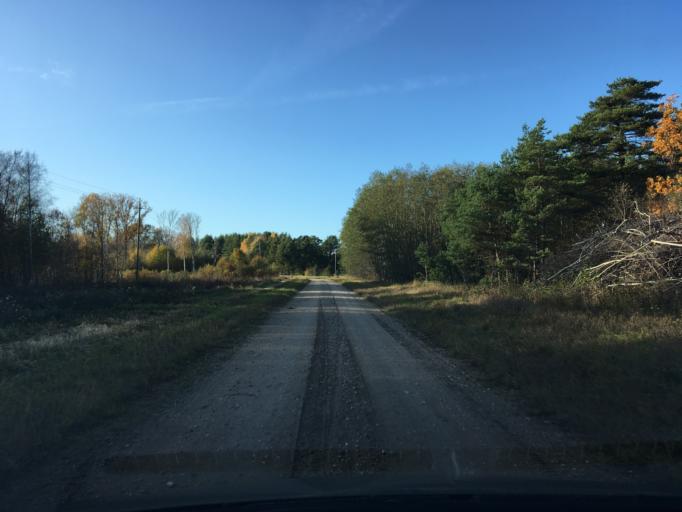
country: EE
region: Laeaene
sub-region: Lihula vald
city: Lihula
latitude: 58.5667
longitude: 23.7650
